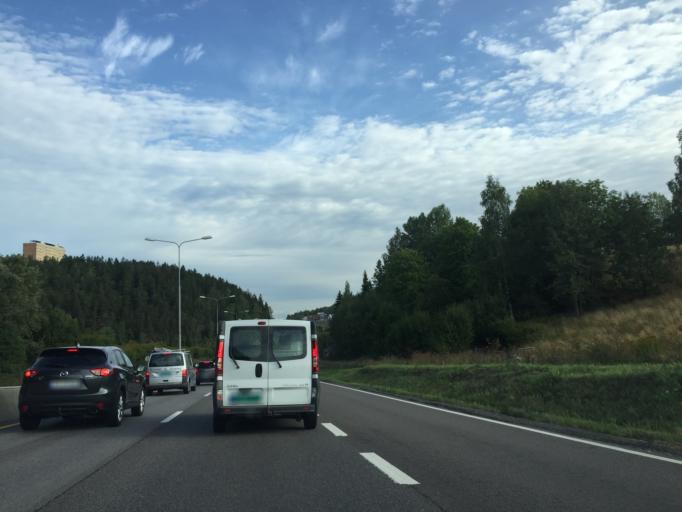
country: NO
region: Akershus
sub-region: Oppegard
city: Kolbotn
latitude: 59.8592
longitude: 10.8312
